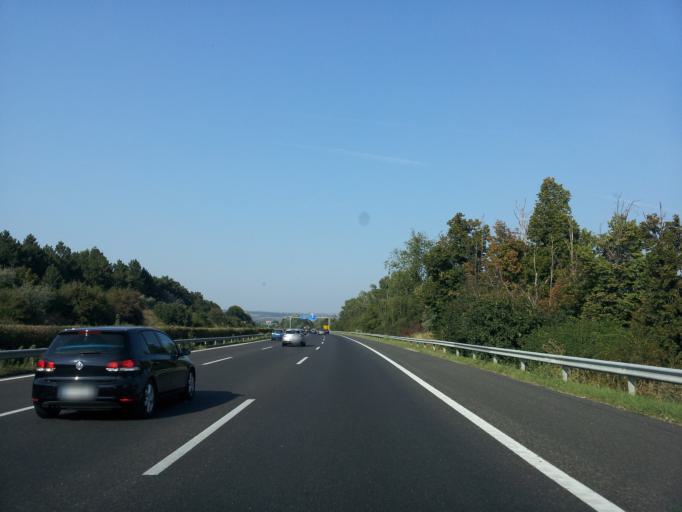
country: HU
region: Pest
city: Tarnok
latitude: 47.3635
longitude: 18.8214
